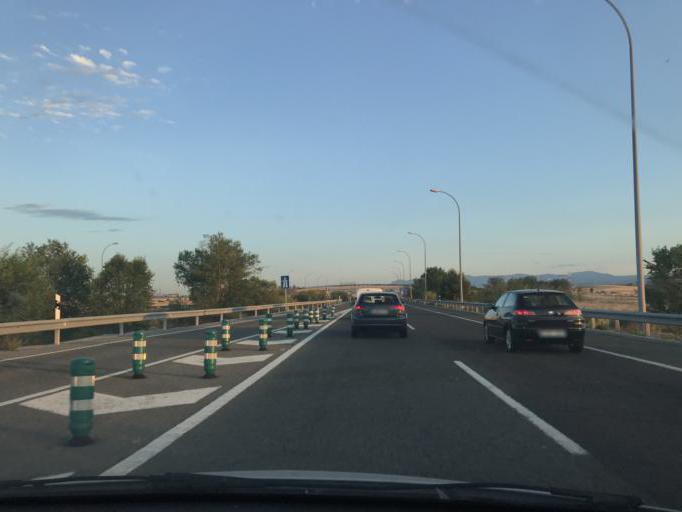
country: ES
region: Madrid
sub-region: Provincia de Madrid
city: San Sebastian de los Reyes
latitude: 40.5480
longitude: -3.5746
